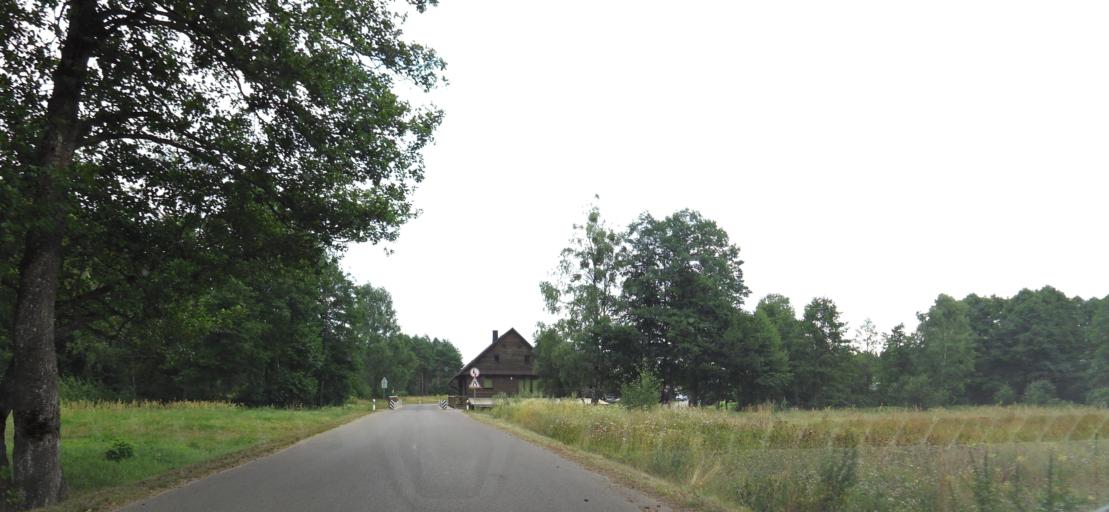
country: LT
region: Alytaus apskritis
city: Druskininkai
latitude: 53.9891
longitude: 24.0440
